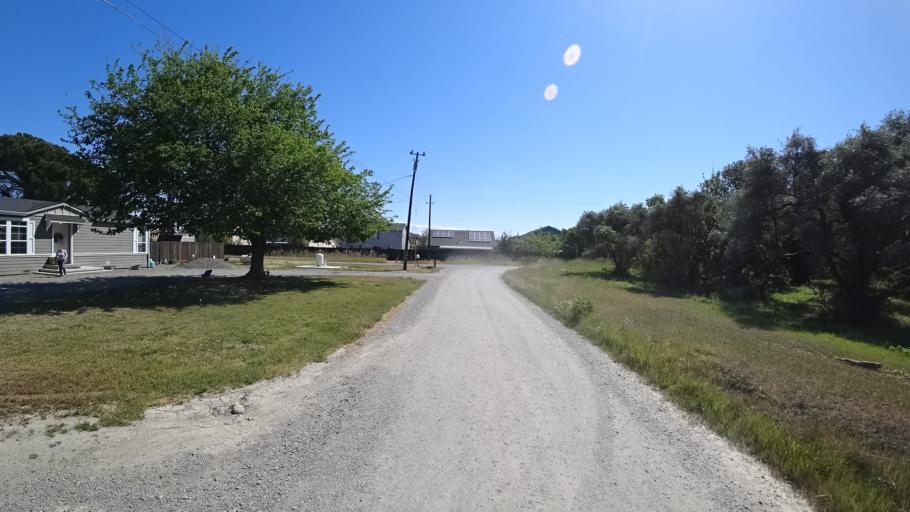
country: US
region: California
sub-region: Glenn County
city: Orland
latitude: 39.7583
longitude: -122.2020
